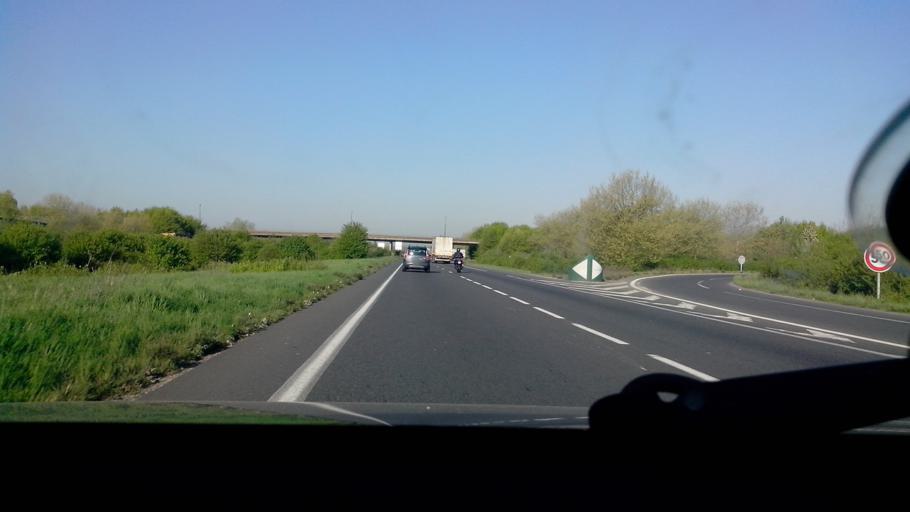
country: FR
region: Ile-de-France
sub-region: Departement de l'Essonne
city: Tigery
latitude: 48.6315
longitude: 2.5174
